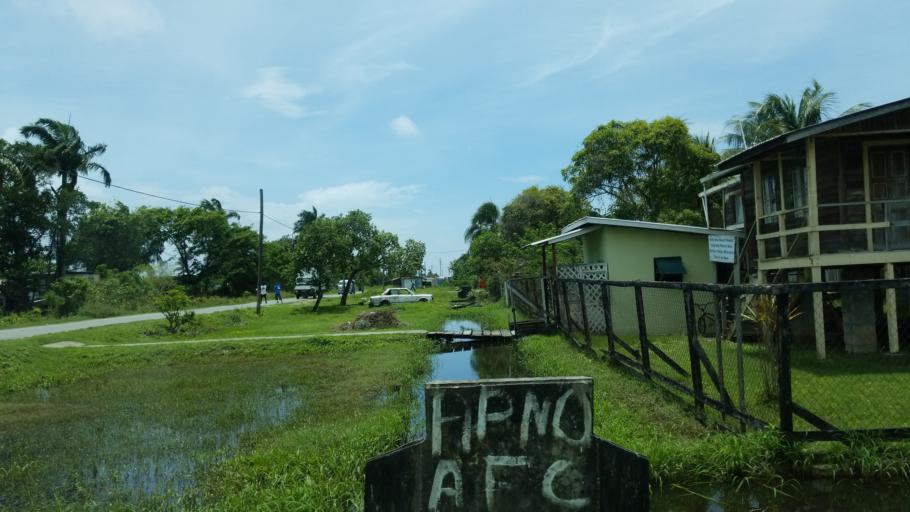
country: GY
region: Demerara-Mahaica
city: Georgetown
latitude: 6.7928
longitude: -58.1258
